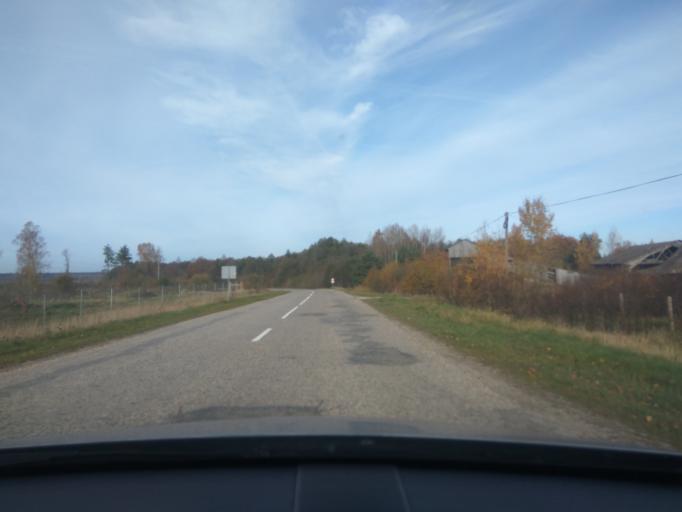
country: LV
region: Alsunga
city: Alsunga
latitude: 56.9816
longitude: 21.5503
